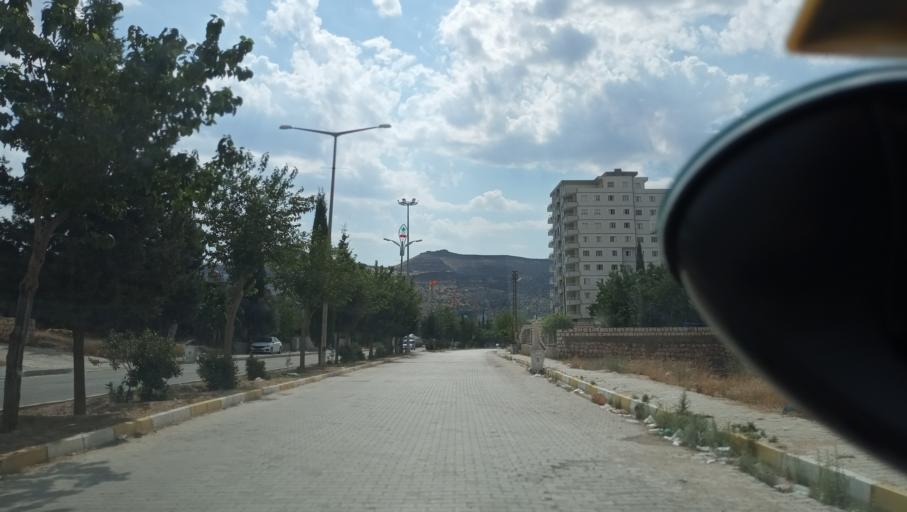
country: TR
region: Mardin
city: Kabala
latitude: 37.3404
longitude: 40.8124
